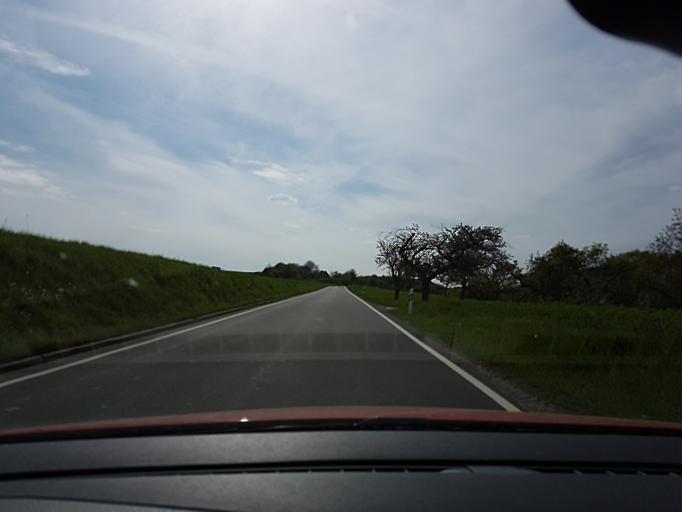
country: DE
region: Bavaria
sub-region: Regierungsbezirk Unterfranken
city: Bergtheim
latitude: 49.9273
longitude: 10.0188
